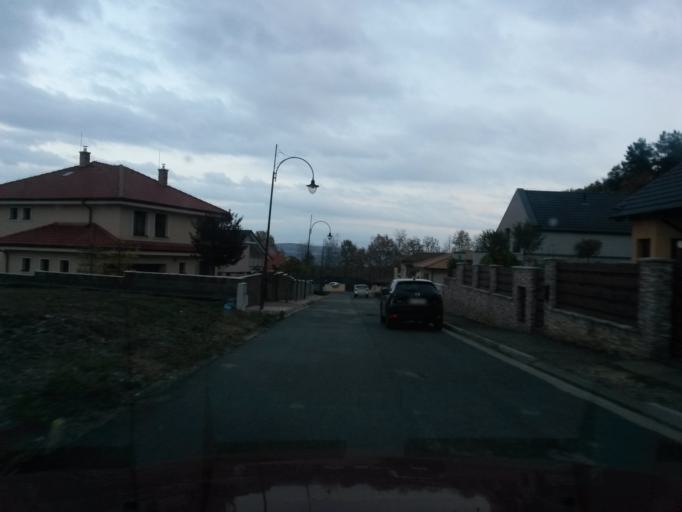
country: SK
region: Kosicky
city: Kosice
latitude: 48.7942
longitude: 21.2947
